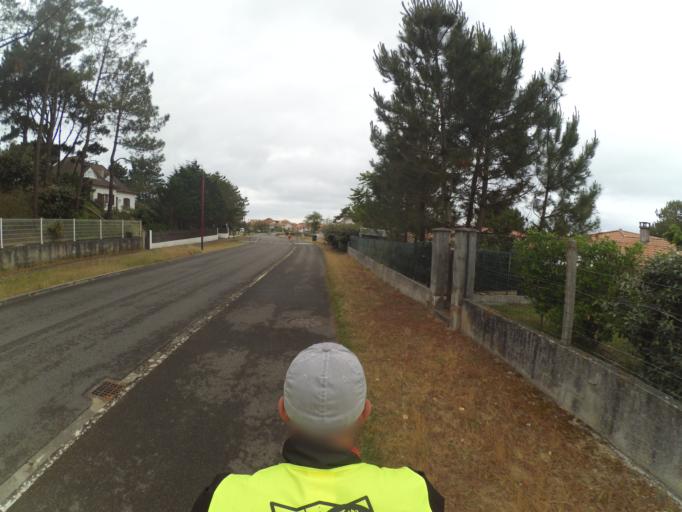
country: FR
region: Aquitaine
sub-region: Departement des Landes
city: Mimizan
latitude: 44.2152
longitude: -1.2902
